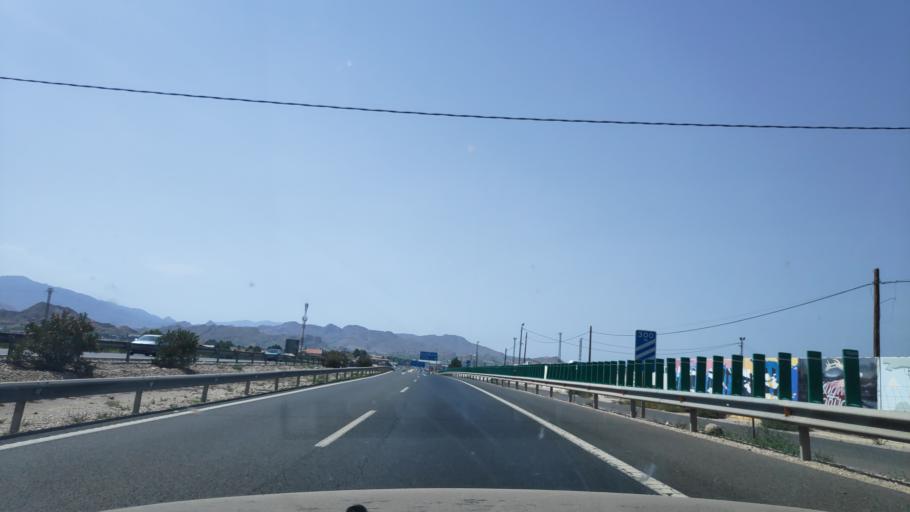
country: ES
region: Murcia
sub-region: Murcia
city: Lorqui
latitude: 38.1195
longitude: -1.2464
